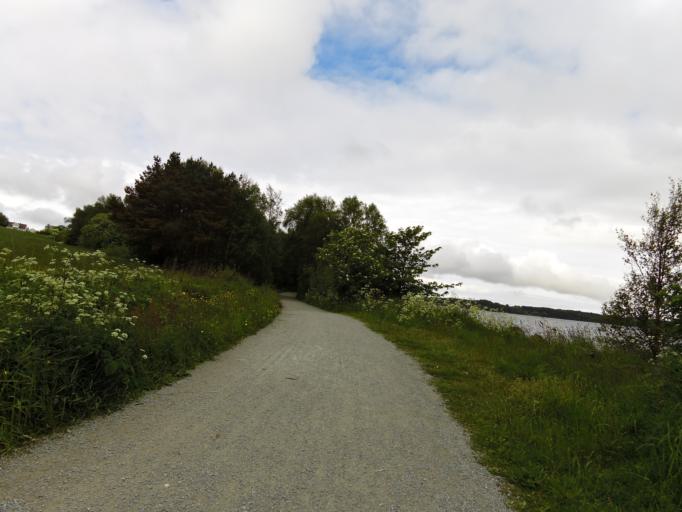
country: NO
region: Rogaland
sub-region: Stavanger
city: Stavanger
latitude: 58.9588
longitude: 5.6737
